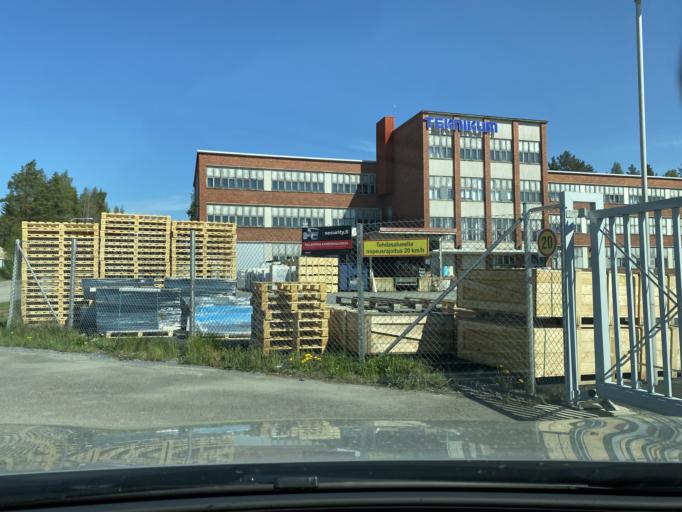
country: FI
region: Pirkanmaa
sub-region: Lounais-Pirkanmaa
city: Vammala
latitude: 61.3523
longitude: 22.8813
